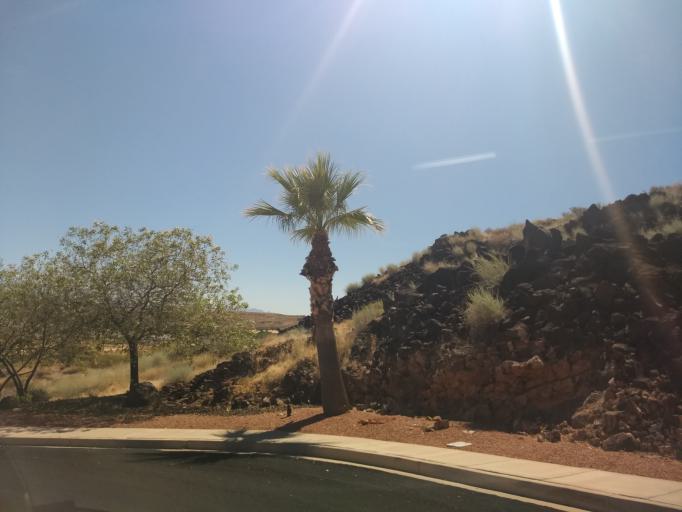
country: US
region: Utah
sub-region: Washington County
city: Washington
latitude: 37.1262
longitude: -113.4987
